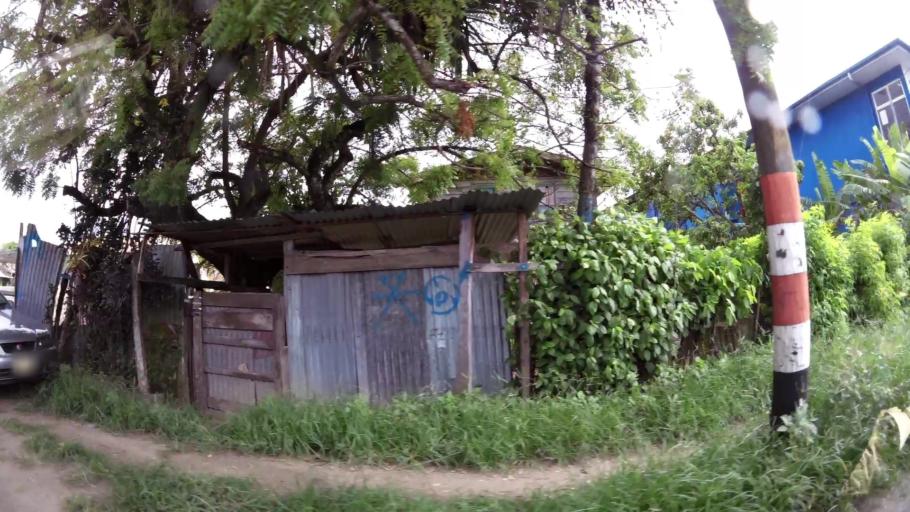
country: SR
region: Paramaribo
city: Paramaribo
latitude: 5.8419
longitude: -55.1947
